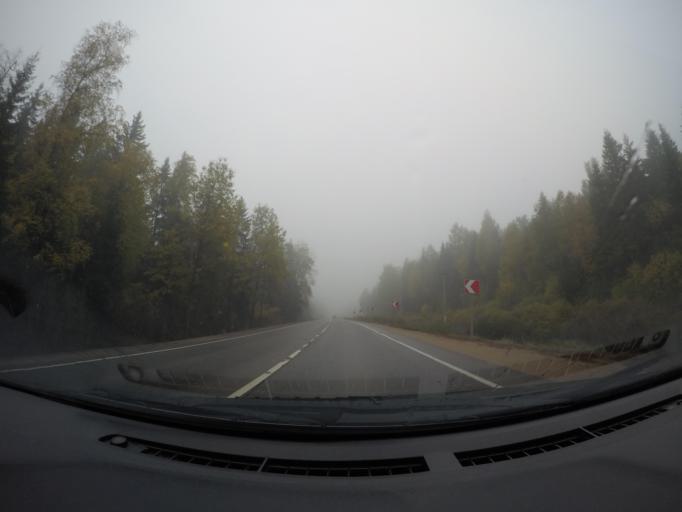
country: RU
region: Moskovskaya
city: Ruza
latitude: 55.7243
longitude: 36.2816
